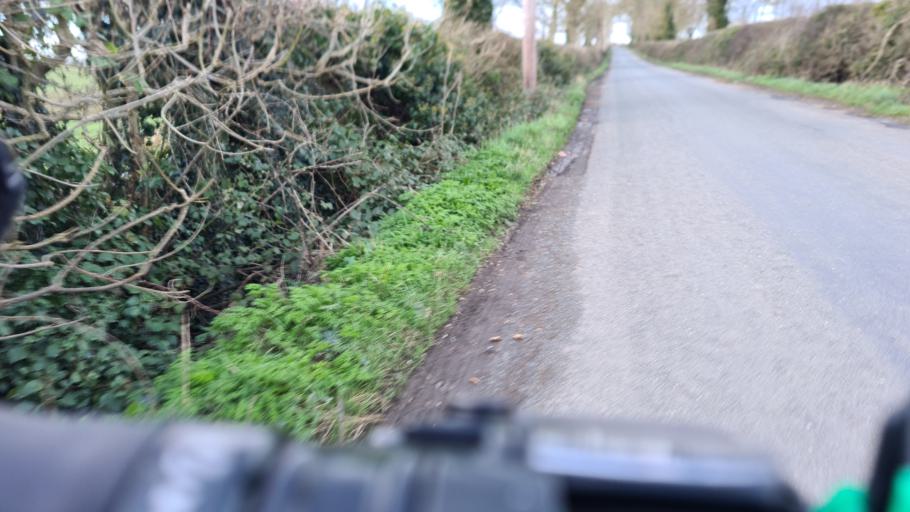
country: IE
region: Leinster
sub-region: Kildare
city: Celbridge
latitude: 53.3467
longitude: -6.5749
